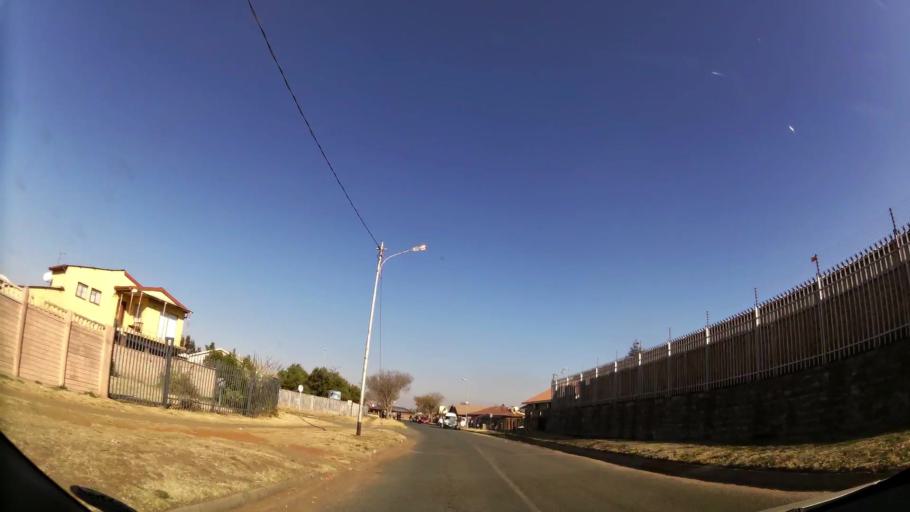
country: ZA
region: Gauteng
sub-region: City of Johannesburg Metropolitan Municipality
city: Roodepoort
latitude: -26.1540
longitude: 27.8528
